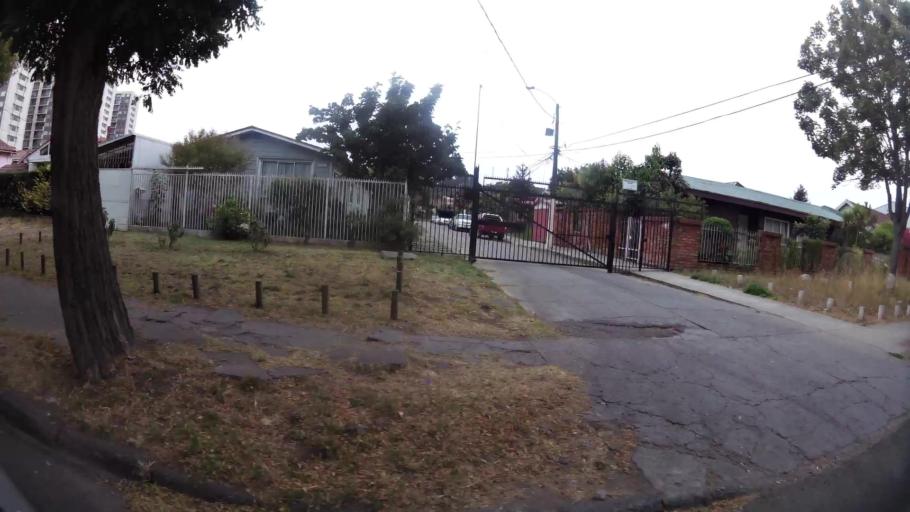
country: CL
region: Biobio
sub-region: Provincia de Concepcion
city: Concepcion
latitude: -36.8136
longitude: -73.0319
